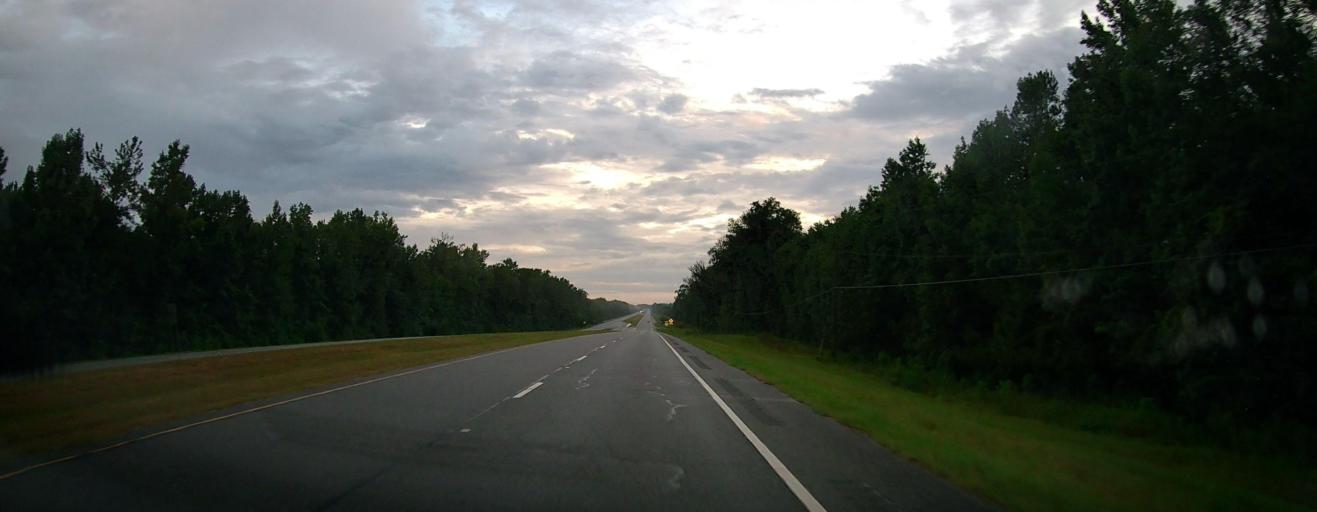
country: US
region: Georgia
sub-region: Lanier County
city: Lakeland
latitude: 30.9330
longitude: -83.0155
